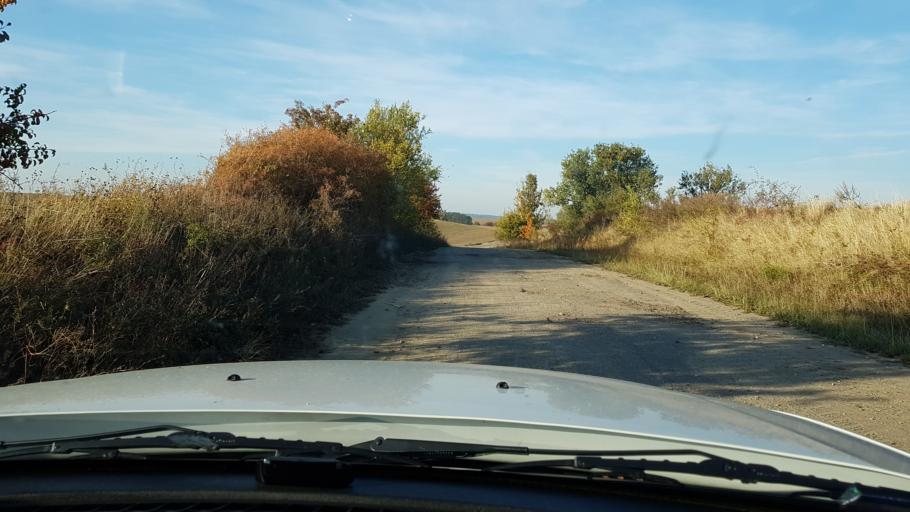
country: PL
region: West Pomeranian Voivodeship
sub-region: Powiat gryfinski
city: Moryn
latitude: 52.8870
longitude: 14.3095
